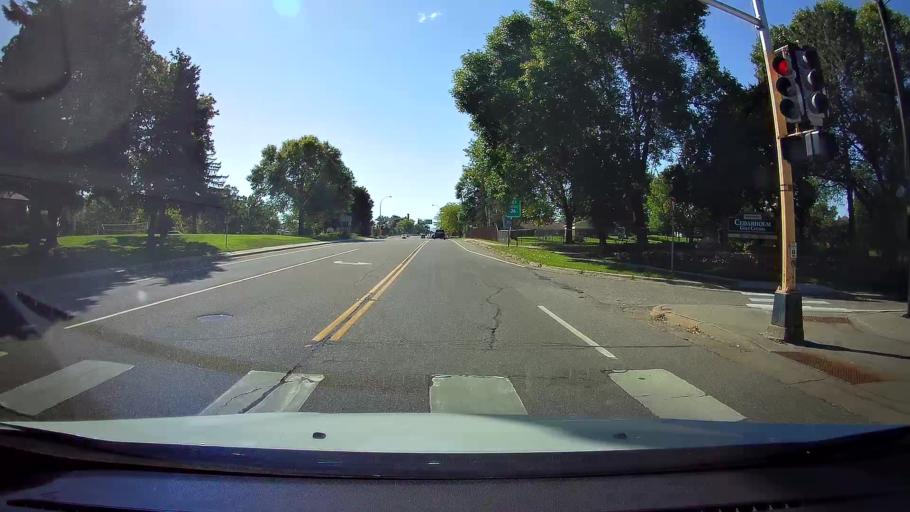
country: US
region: Minnesota
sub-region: Ramsey County
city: Roseville
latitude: 45.0134
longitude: -93.1568
